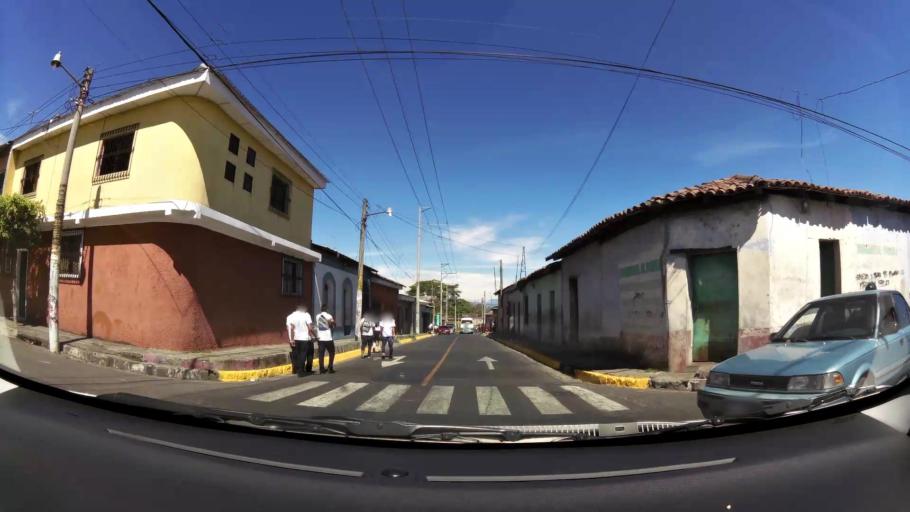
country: SV
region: La Libertad
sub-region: Distrito de Quezaltepeque
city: Quezaltepeque
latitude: 13.8340
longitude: -89.2748
